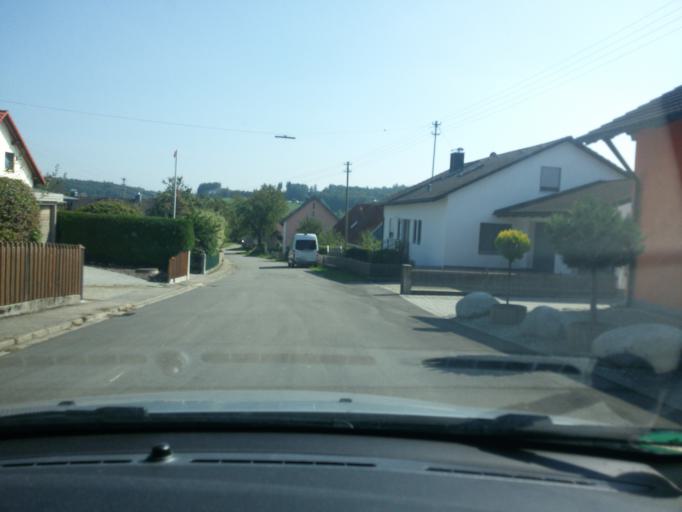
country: DE
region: Bavaria
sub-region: Swabia
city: Scherstetten
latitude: 48.1805
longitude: 10.6366
